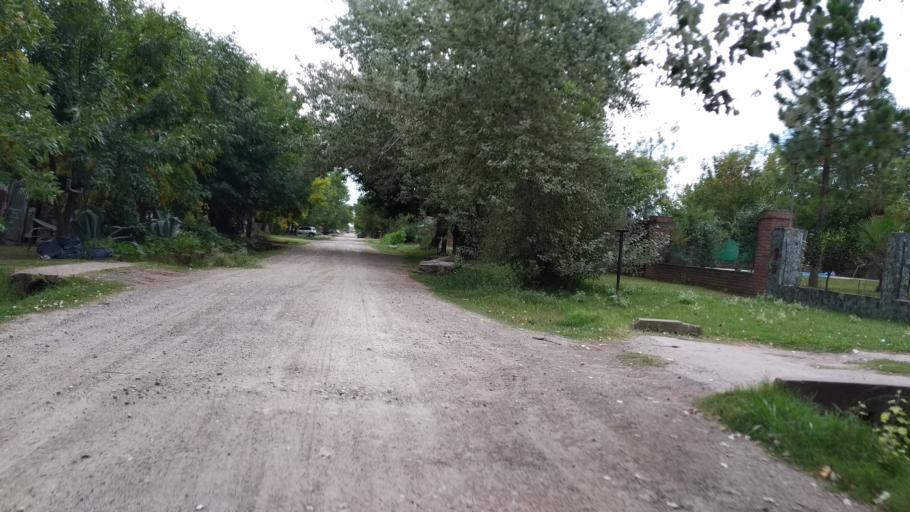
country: AR
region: Santa Fe
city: Funes
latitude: -32.9296
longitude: -60.8026
